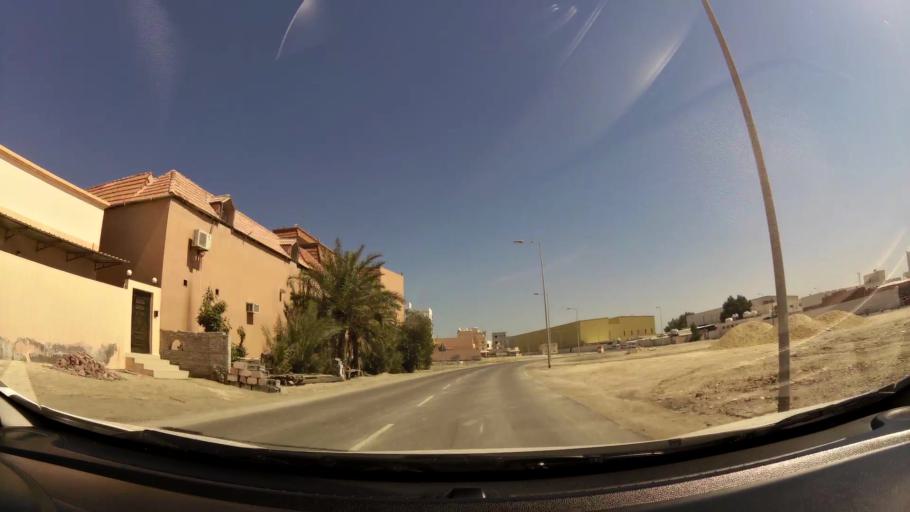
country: BH
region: Muharraq
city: Al Muharraq
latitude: 26.2778
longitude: 50.6391
